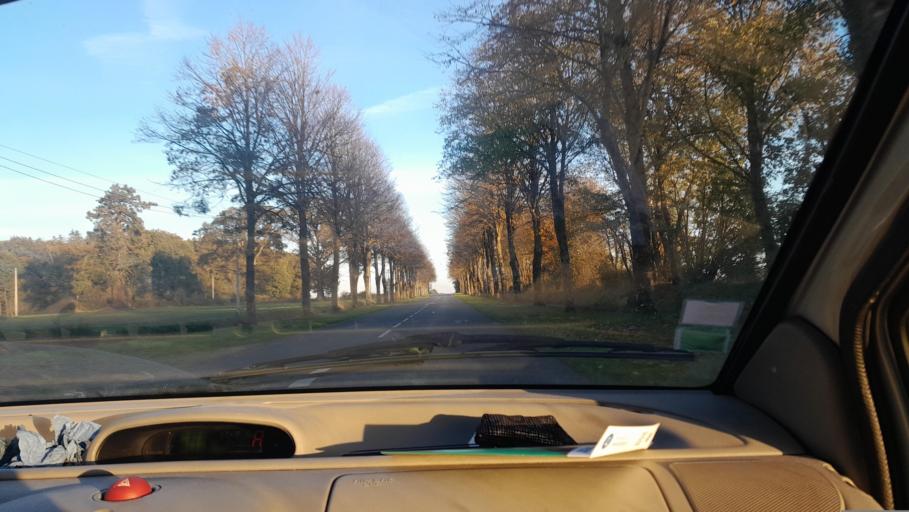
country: FR
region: Brittany
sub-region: Departement d'Ille-et-Vilaine
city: Argentre-du-Plessis
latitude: 47.9702
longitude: -1.1097
